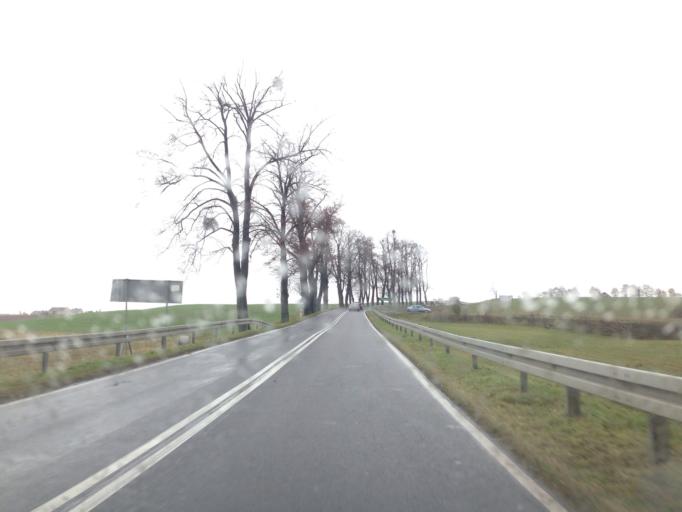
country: PL
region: Warmian-Masurian Voivodeship
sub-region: Powiat nowomiejski
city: Biskupiec
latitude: 53.6050
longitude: 19.3947
